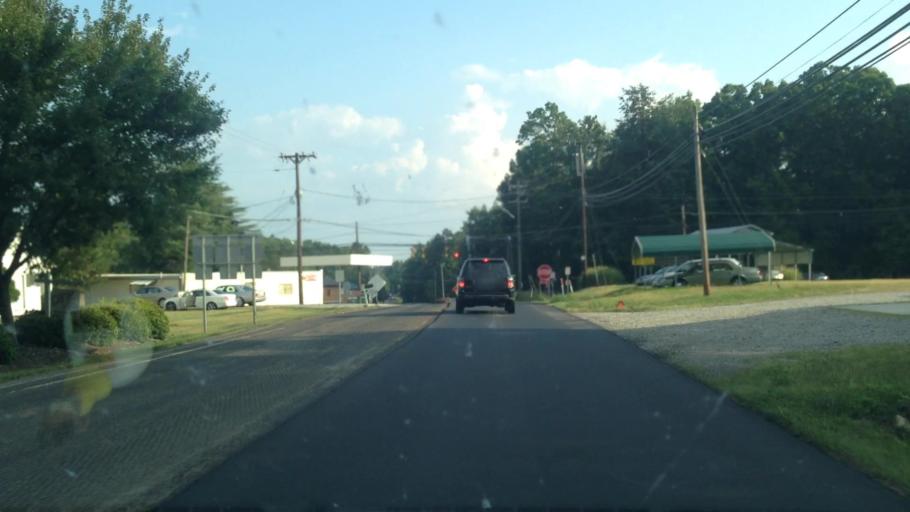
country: US
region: North Carolina
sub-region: Davidson County
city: Wallburg
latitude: 36.0205
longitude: -80.0598
